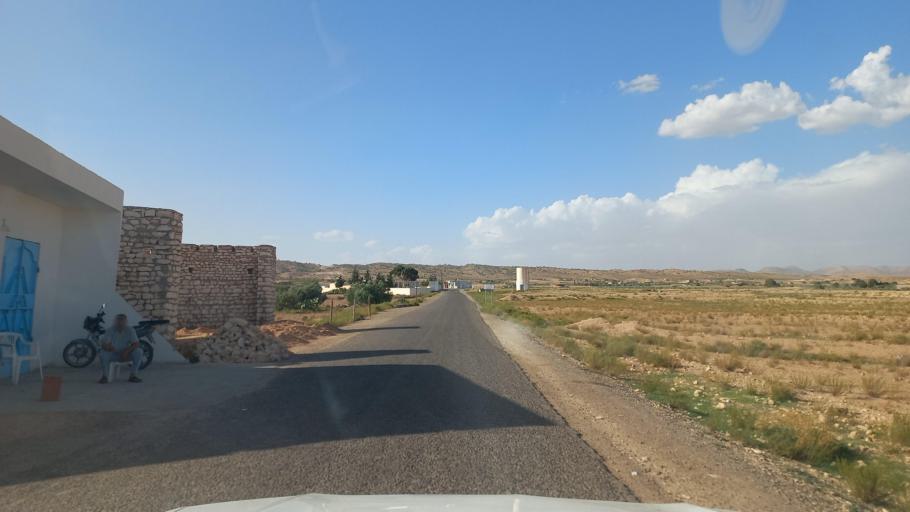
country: TN
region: Al Qasrayn
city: Sbiba
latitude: 35.3418
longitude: 8.9915
